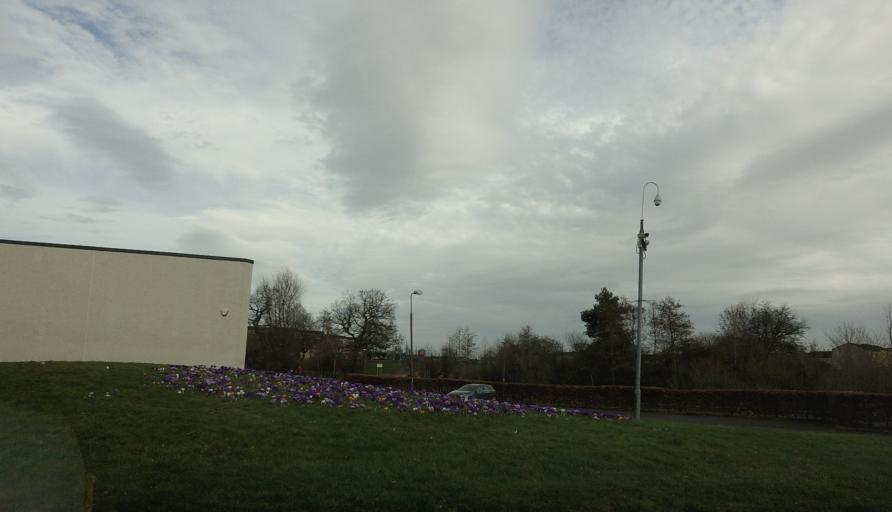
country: GB
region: Scotland
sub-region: West Lothian
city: Mid Calder
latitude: 55.8810
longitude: -3.5047
